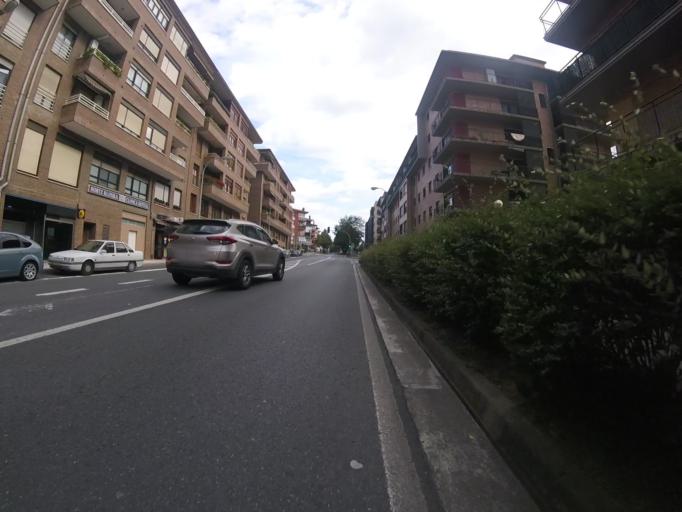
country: ES
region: Basque Country
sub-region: Provincia de Guipuzcoa
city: Urnieta
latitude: 43.2495
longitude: -1.9916
